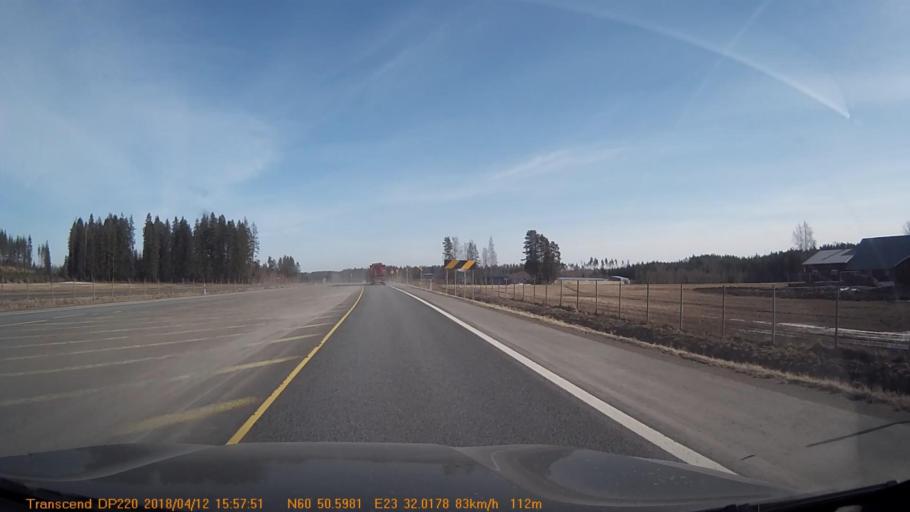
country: FI
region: Haeme
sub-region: Forssa
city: Jokioinen
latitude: 60.8427
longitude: 23.5346
